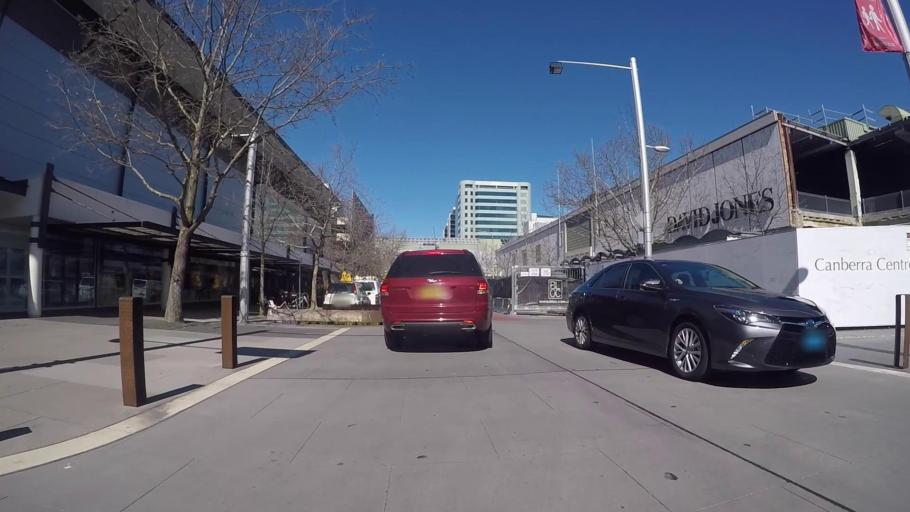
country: AU
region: Australian Capital Territory
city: Canberra
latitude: -35.2791
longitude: 149.1333
